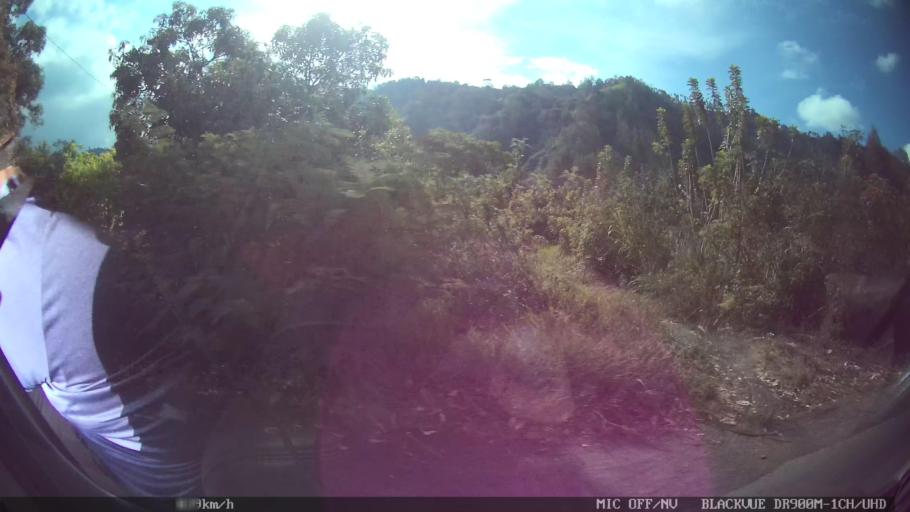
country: ID
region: Bali
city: Banjar Kedisan
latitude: -8.2218
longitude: 115.3619
